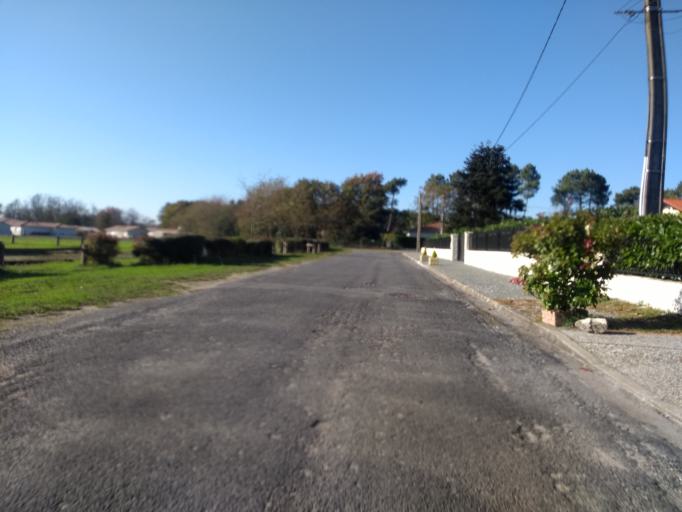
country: FR
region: Aquitaine
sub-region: Departement de la Gironde
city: Ayguemorte-les-Graves
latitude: 44.7122
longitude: -0.4737
